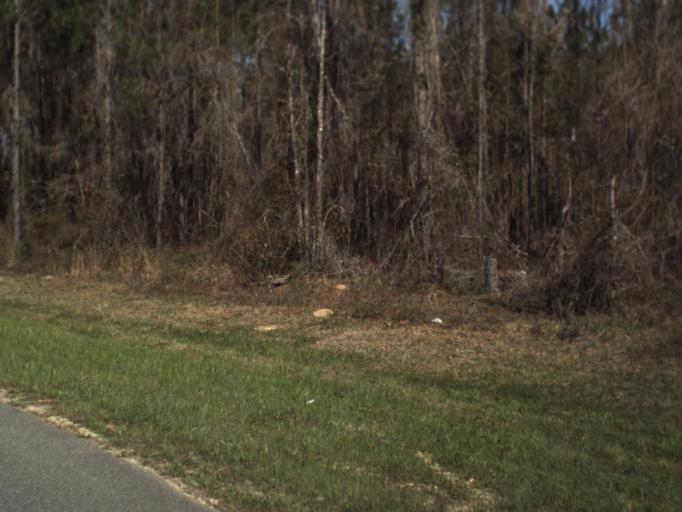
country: US
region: Florida
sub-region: Calhoun County
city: Blountstown
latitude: 30.3240
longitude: -85.1273
